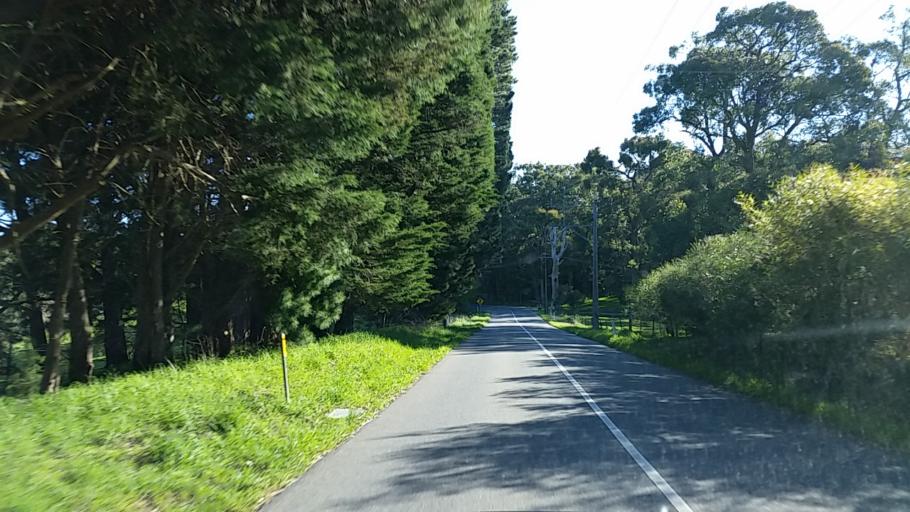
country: AU
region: South Australia
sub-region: Adelaide Hills
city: Adelaide Hills
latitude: -34.9338
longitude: 138.7439
